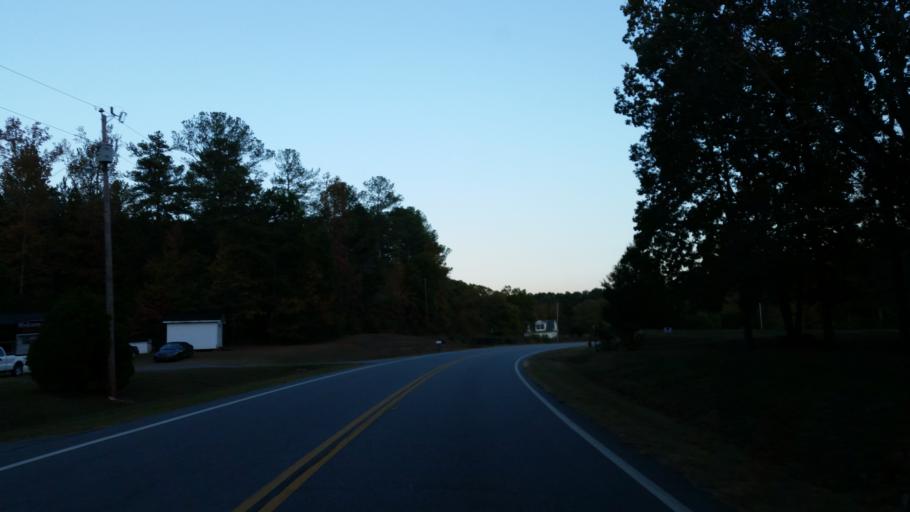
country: US
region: Georgia
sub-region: Gordon County
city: Calhoun
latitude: 34.6084
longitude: -85.0428
